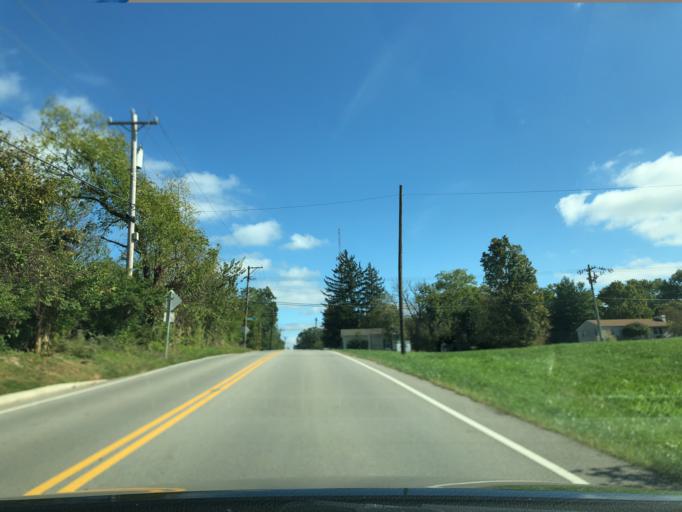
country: US
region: Ohio
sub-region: Hamilton County
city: The Village of Indian Hill
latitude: 39.2443
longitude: -84.2861
